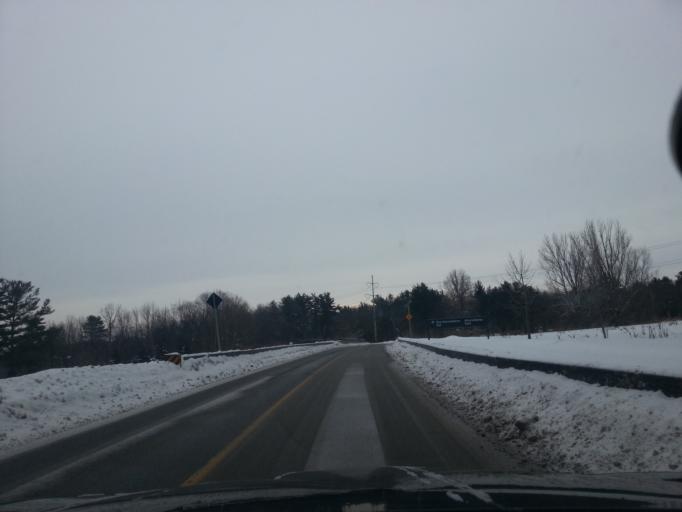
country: CA
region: Ontario
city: Ottawa
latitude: 45.4336
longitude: -75.7506
